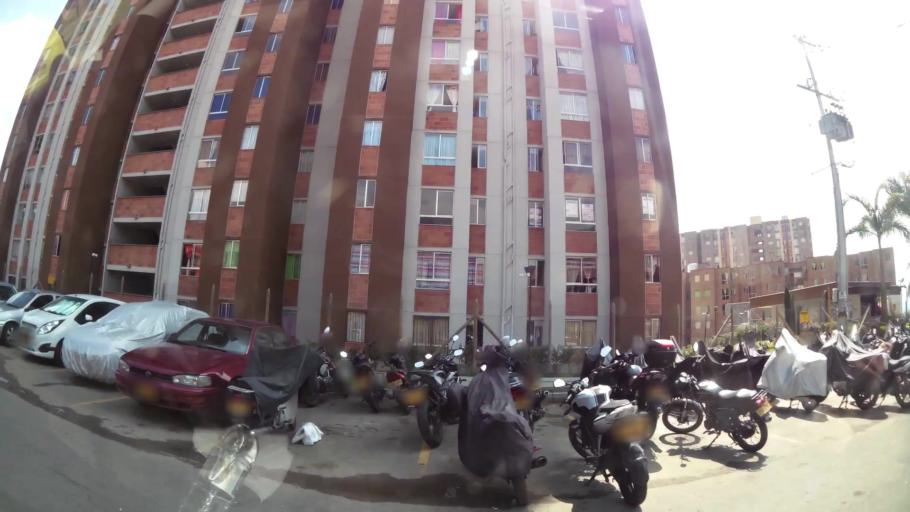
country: CO
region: Antioquia
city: La Estrella
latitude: 6.1754
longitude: -75.6480
